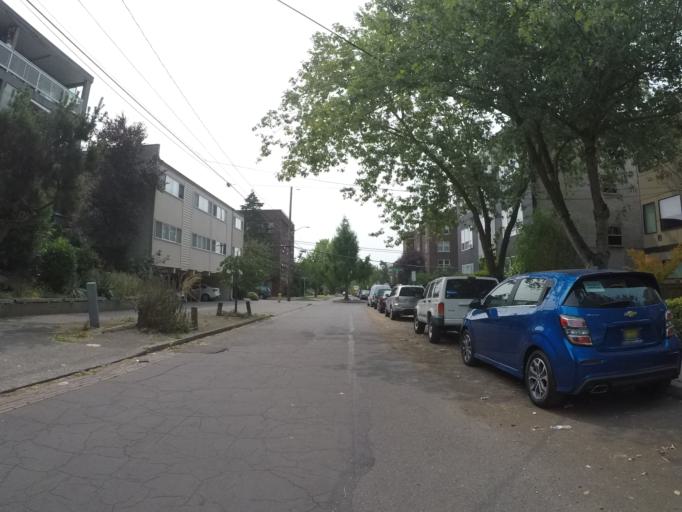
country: US
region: Washington
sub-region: King County
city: Seattle
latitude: 47.6192
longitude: -122.3156
